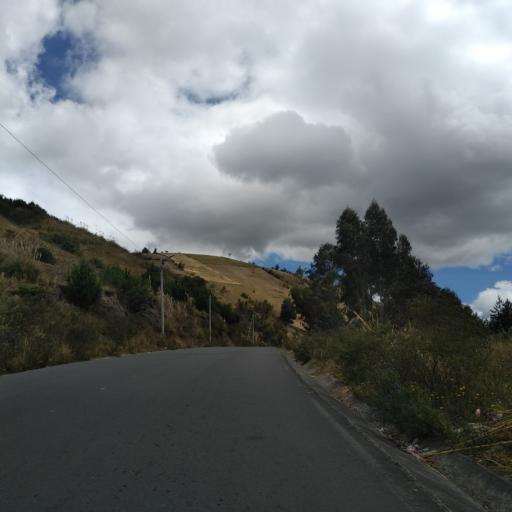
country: EC
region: Cotopaxi
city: Saquisili
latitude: -0.7506
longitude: -78.7237
